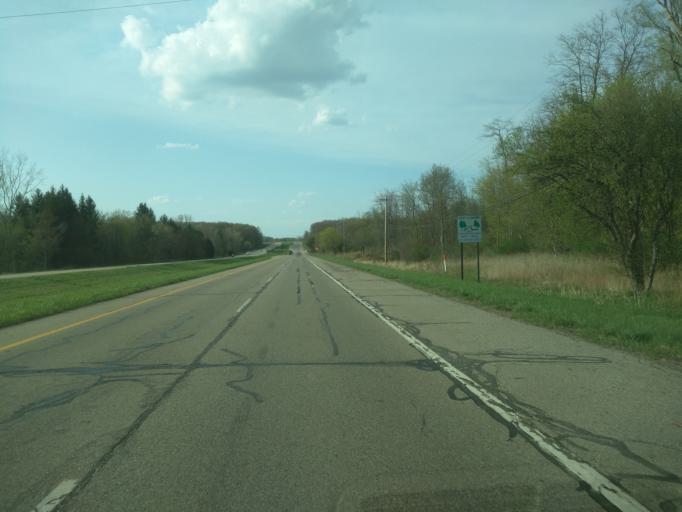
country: US
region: Michigan
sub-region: Eaton County
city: Dimondale
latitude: 42.6269
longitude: -84.6226
